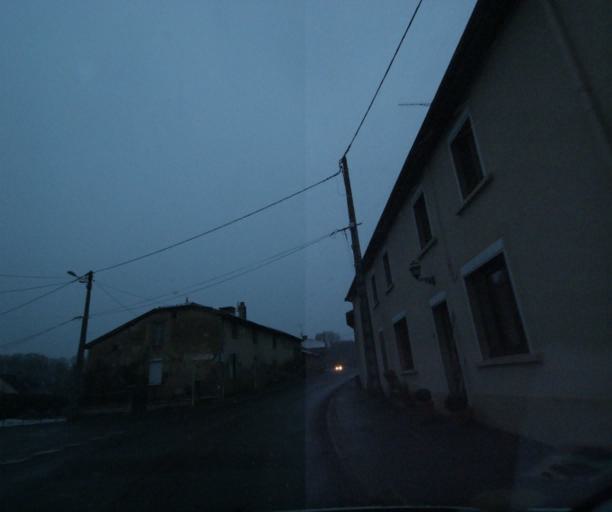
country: FR
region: Champagne-Ardenne
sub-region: Departement de la Haute-Marne
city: Wassy
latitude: 48.4399
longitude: 4.9579
